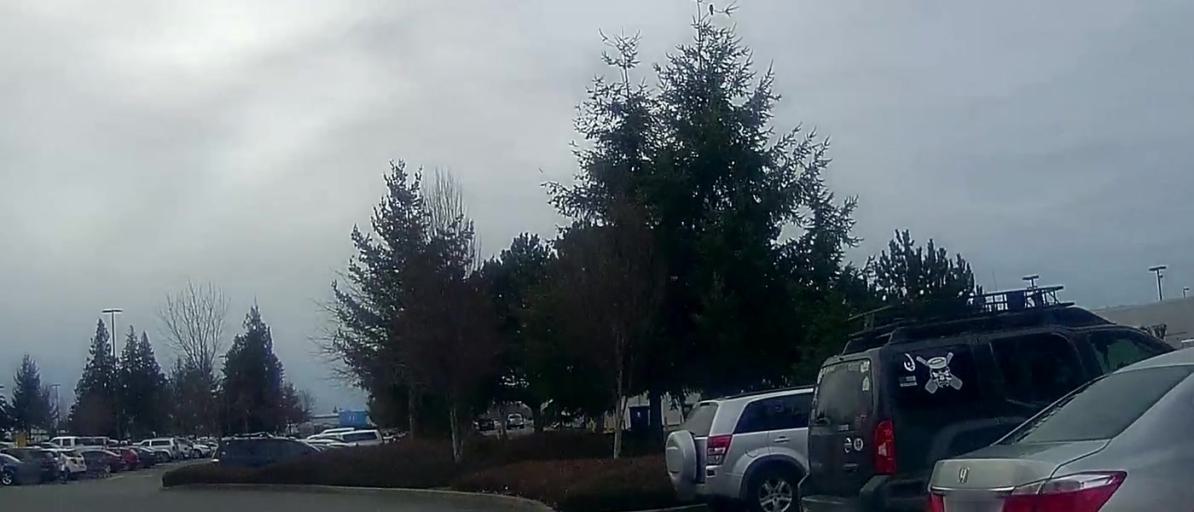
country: US
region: Washington
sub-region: Skagit County
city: Mount Vernon
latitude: 48.4317
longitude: -122.2904
